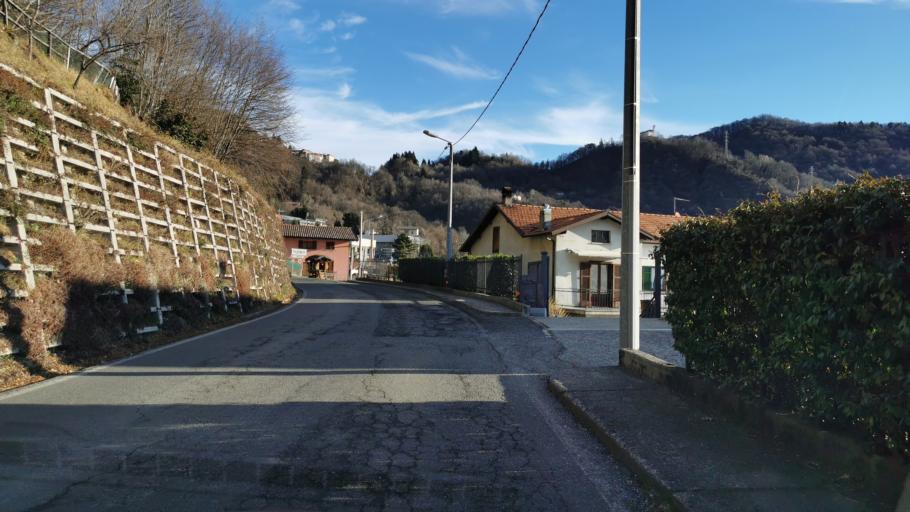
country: IT
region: Lombardy
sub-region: Provincia di Como
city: Plesio
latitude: 46.0448
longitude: 9.2265
